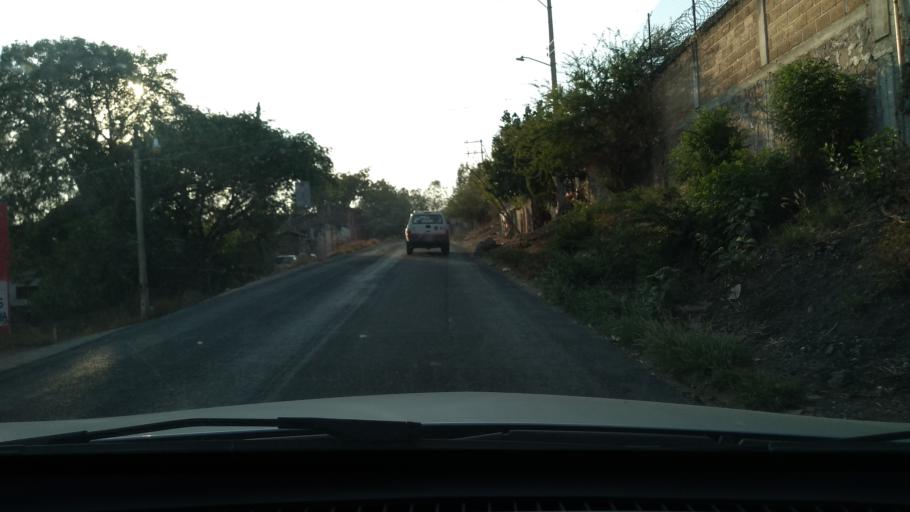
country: MX
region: Morelos
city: Puente de Ixtla
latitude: 18.6154
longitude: -99.3145
